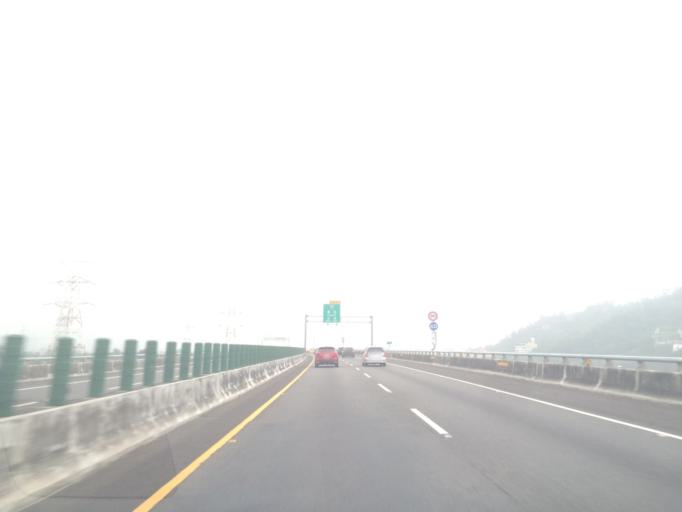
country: TW
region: Taiwan
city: Zhongxing New Village
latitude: 24.0086
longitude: 120.7052
